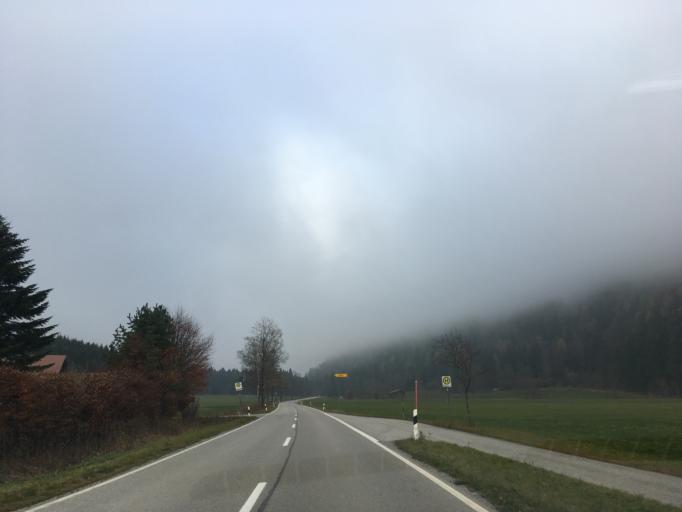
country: AT
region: Tyrol
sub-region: Politischer Bezirk Kufstein
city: Rettenschoss
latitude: 47.7048
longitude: 12.2778
